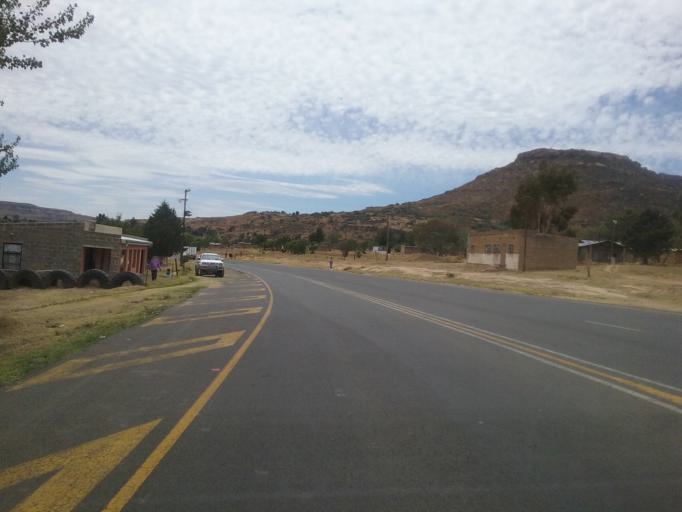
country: LS
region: Maseru
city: Nako
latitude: -29.6445
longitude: 27.4747
